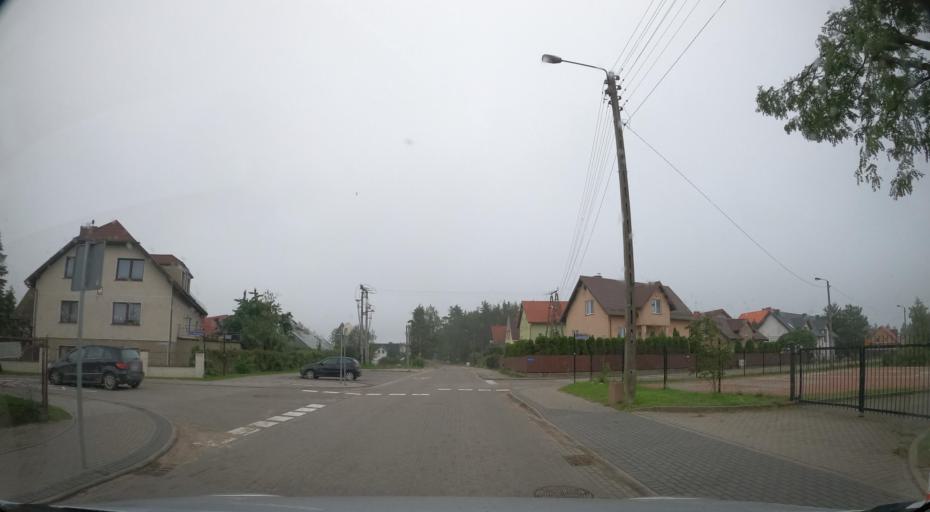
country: PL
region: Pomeranian Voivodeship
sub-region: Powiat kartuski
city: Chwaszczyno
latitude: 54.4395
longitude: 18.4184
